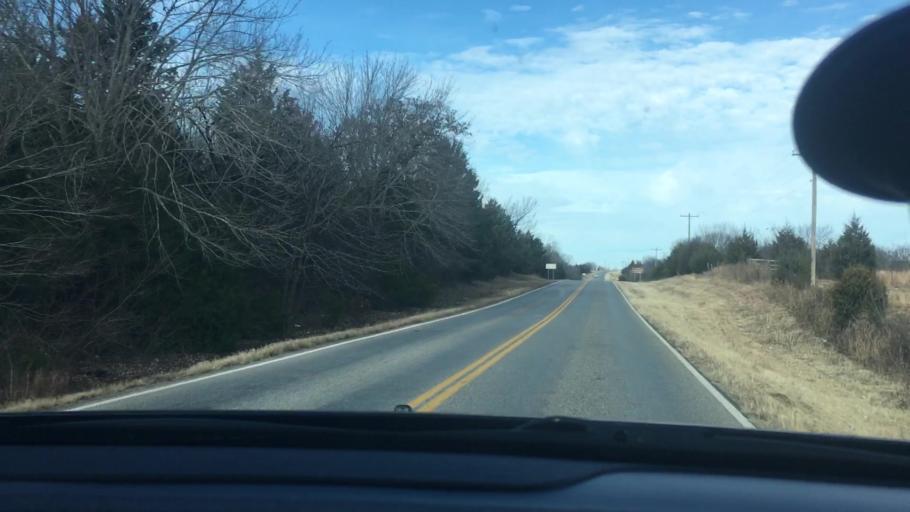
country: US
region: Oklahoma
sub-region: Seminole County
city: Konawa
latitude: 34.9666
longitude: -96.7709
